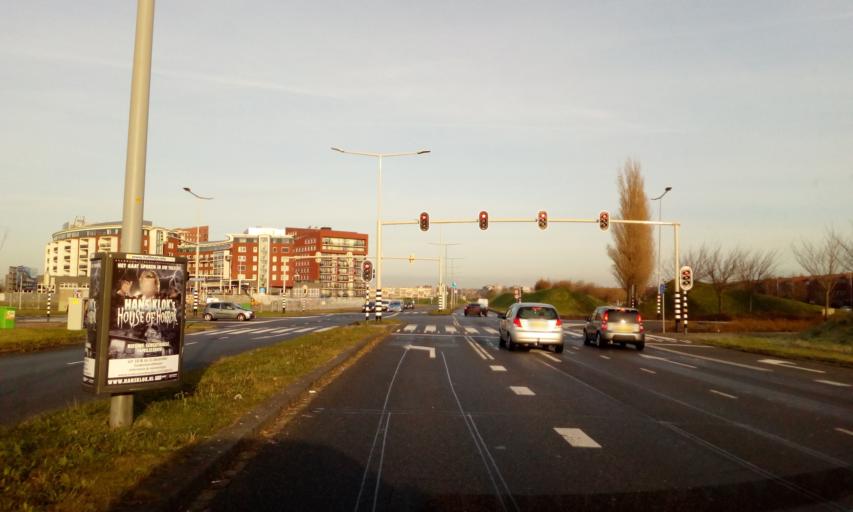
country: NL
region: South Holland
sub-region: Gemeente Den Haag
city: Ypenburg
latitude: 52.0614
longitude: 4.4063
